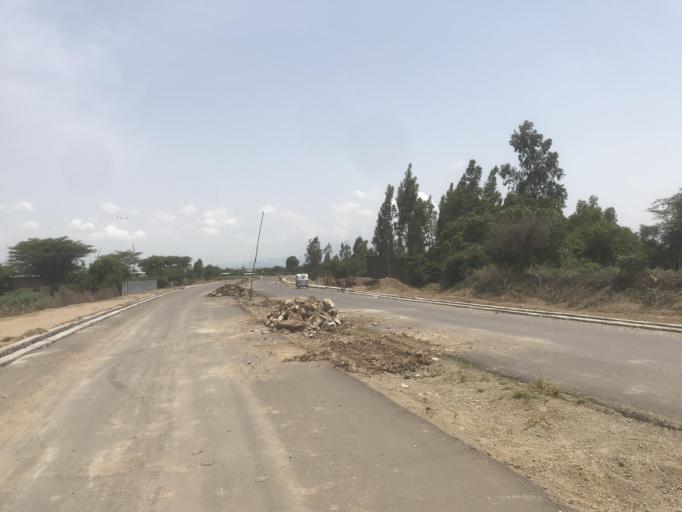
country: ET
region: Oromiya
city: Mojo
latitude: 8.2919
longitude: 38.9414
